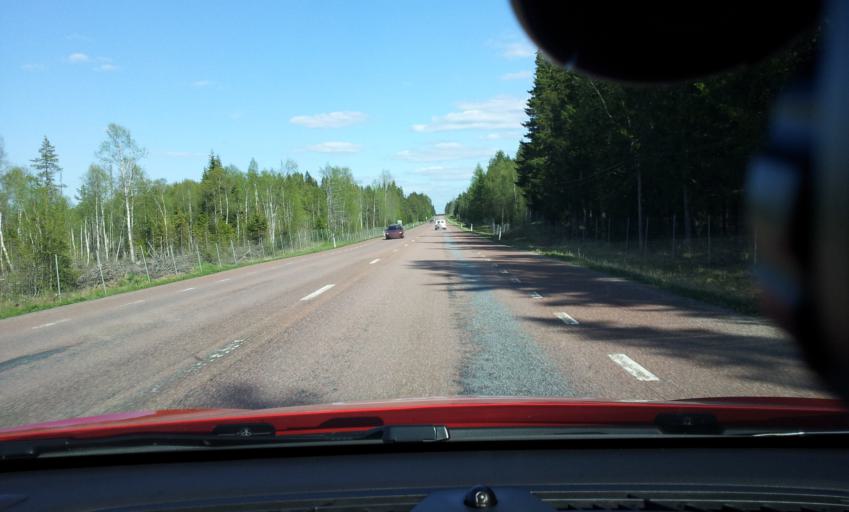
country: SE
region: Jaemtland
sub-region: Krokoms Kommun
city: Krokom
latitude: 63.3256
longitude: 14.3120
